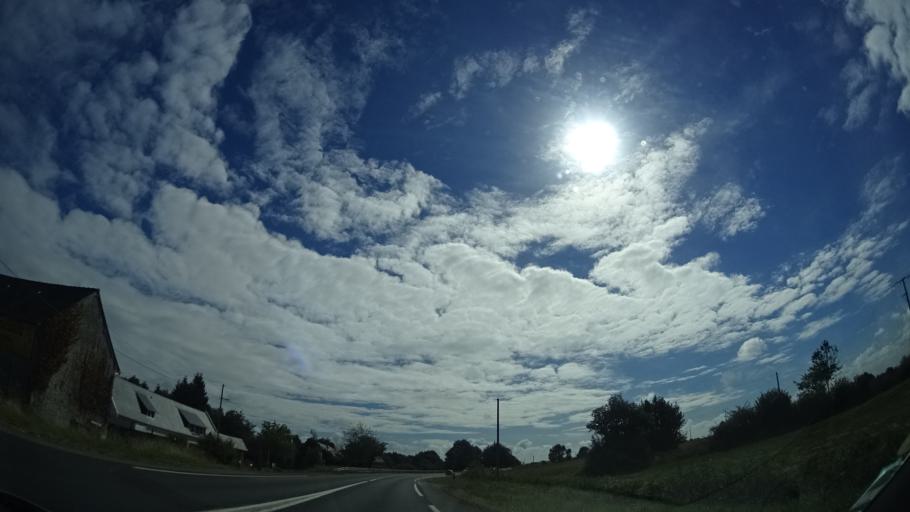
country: FR
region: Pays de la Loire
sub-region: Departement de la Mayenne
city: Port-Brillet
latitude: 48.0758
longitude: -0.9746
